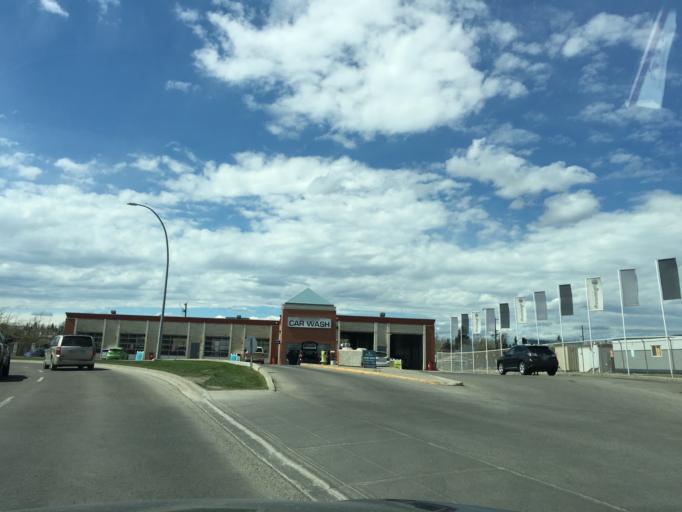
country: CA
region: Alberta
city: Calgary
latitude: 50.9056
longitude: -114.0688
